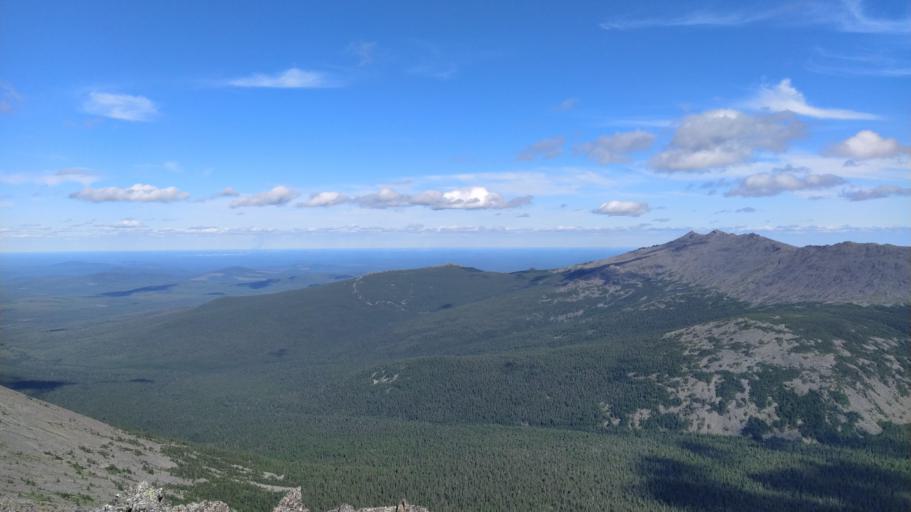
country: RU
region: Sverdlovsk
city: Karpinsk
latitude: 59.6503
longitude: 59.1781
